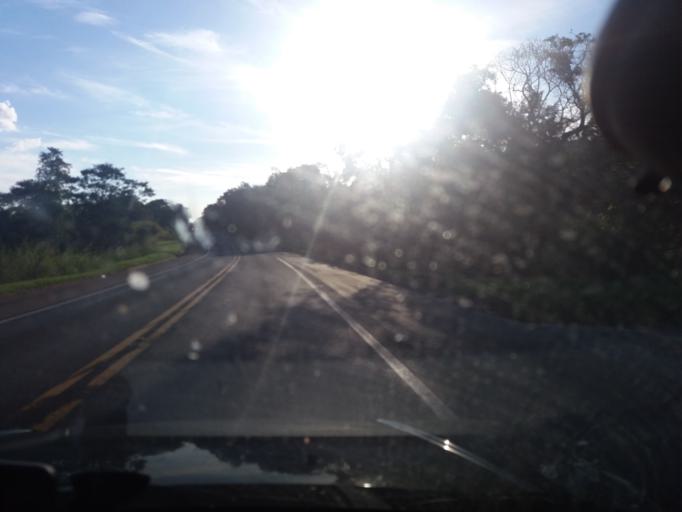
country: BR
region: Sao Paulo
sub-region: Buri
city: Buri
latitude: -23.9326
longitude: -48.6362
